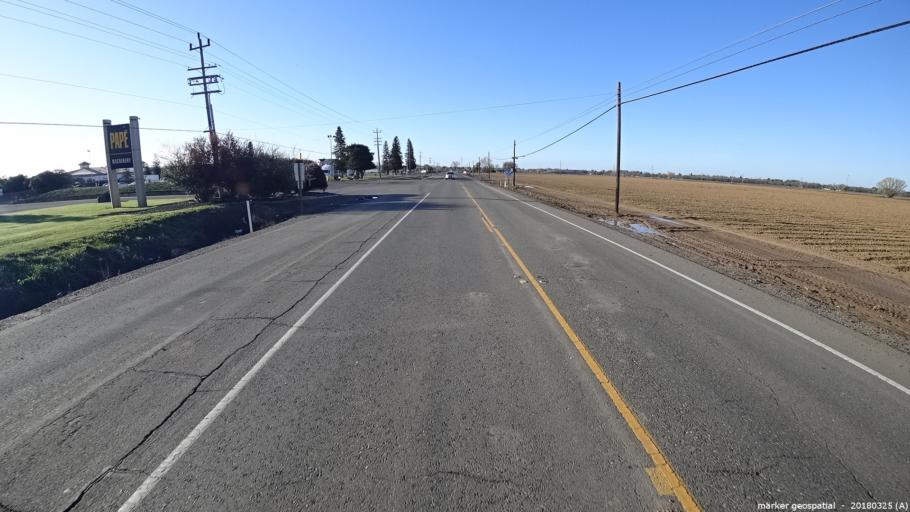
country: US
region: California
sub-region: Yolo County
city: West Sacramento
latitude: 38.6188
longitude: -121.5395
